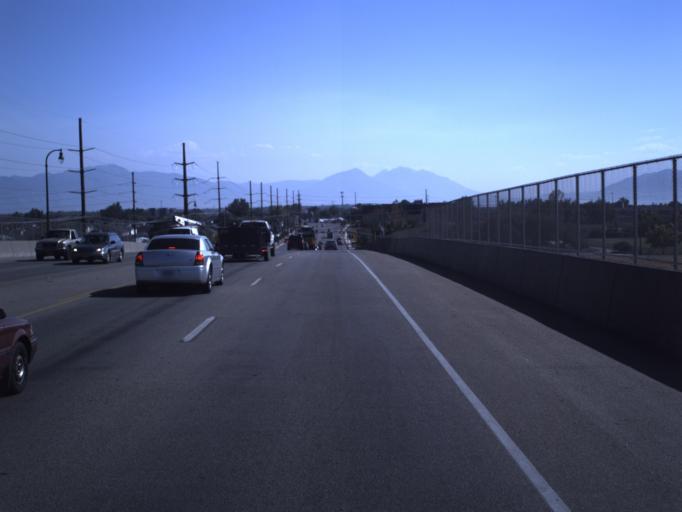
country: US
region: Utah
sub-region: Utah County
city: Orem
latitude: 40.2920
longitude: -111.7341
